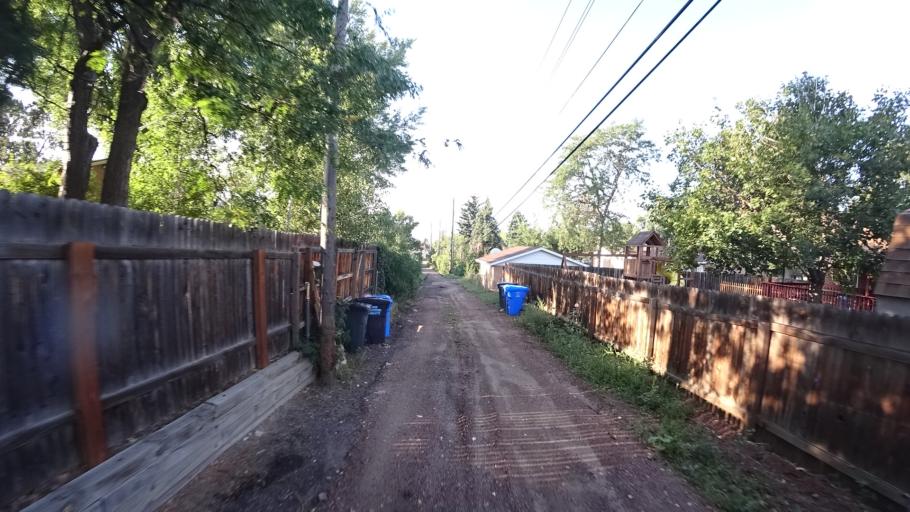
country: US
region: Colorado
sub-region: El Paso County
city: Colorado Springs
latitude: 38.8906
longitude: -104.8091
